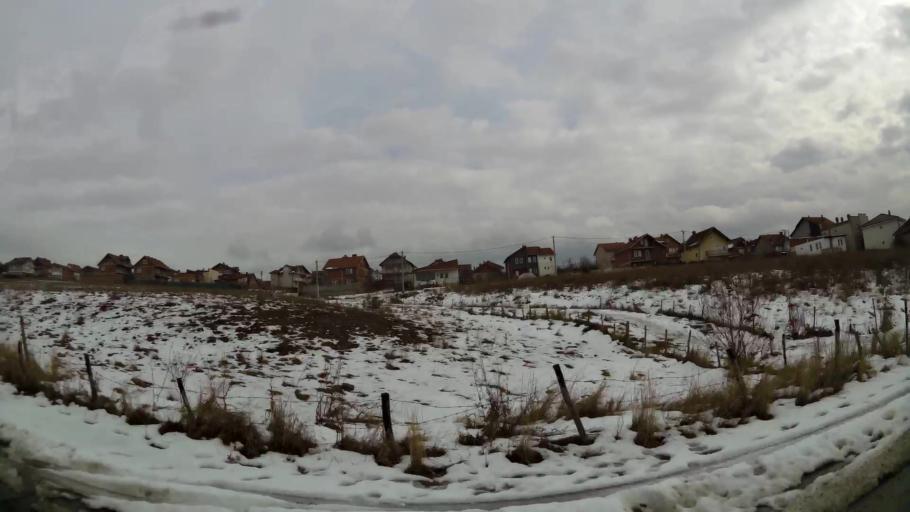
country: XK
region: Pristina
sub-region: Komuna e Prishtines
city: Pristina
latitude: 42.6861
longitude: 21.1627
